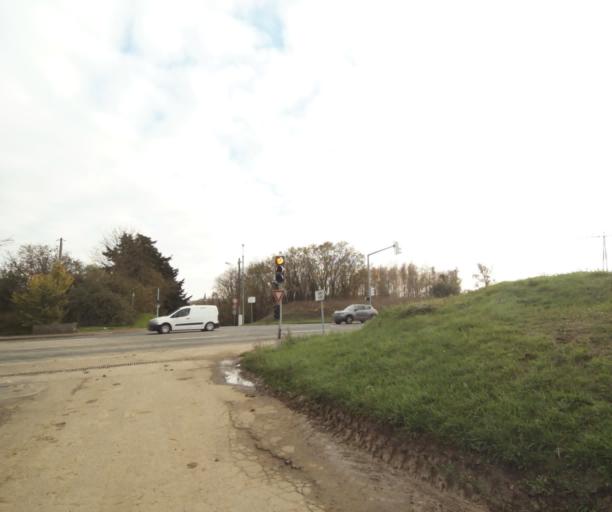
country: FR
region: Ile-de-France
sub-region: Departement du Val-d'Oise
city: Le Thillay
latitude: 49.0014
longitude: 2.4643
